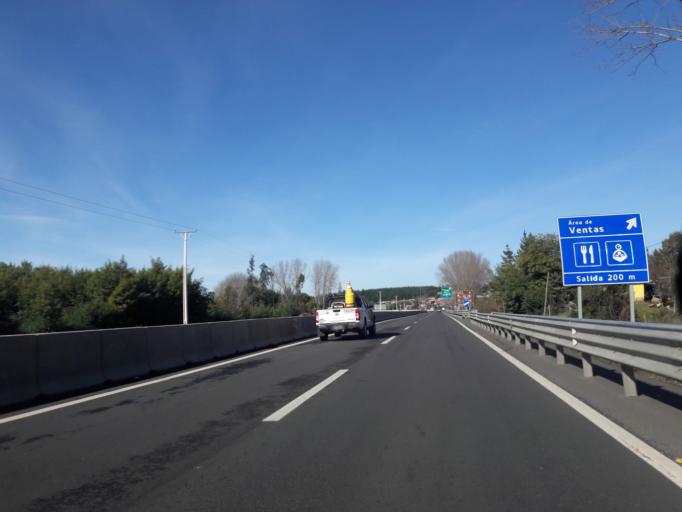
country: CL
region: Biobio
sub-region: Provincia de Biobio
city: Yumbel
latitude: -36.9811
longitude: -72.6311
